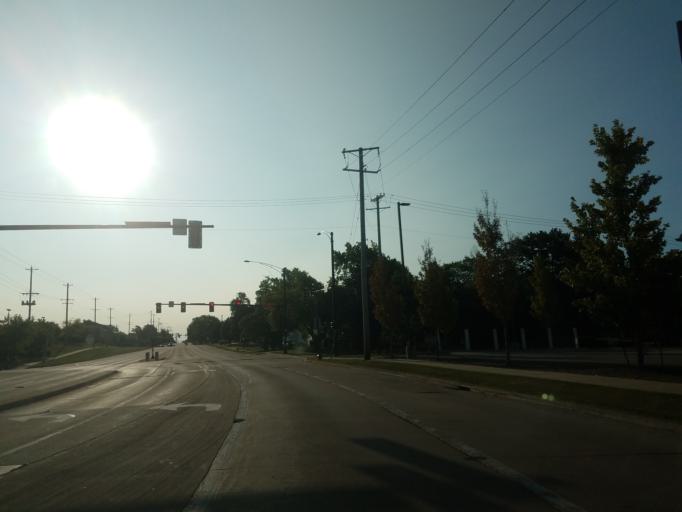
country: US
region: Illinois
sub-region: McLean County
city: Normal
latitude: 40.5316
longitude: -88.9939
